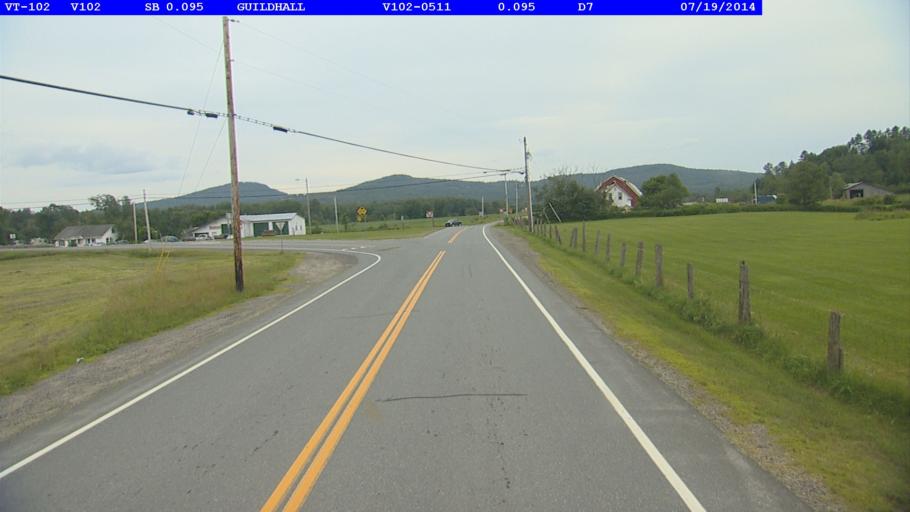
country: US
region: New Hampshire
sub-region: Coos County
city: Lancaster
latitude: 44.4969
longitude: -71.5963
